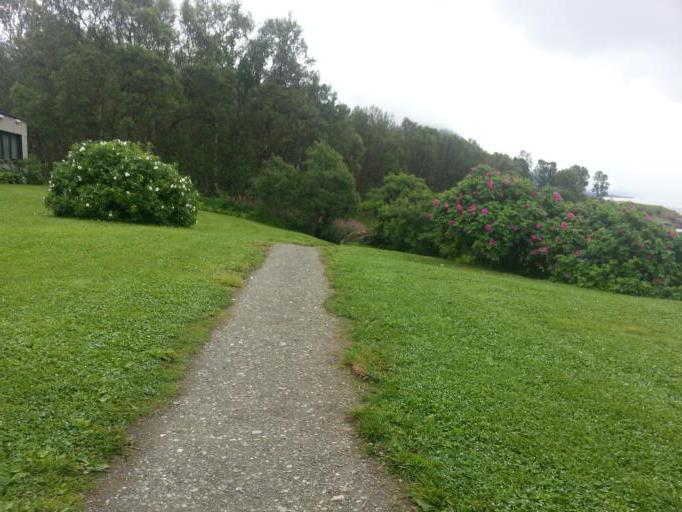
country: NO
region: Troms
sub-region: Tromso
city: Tromso
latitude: 69.6341
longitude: 18.9045
